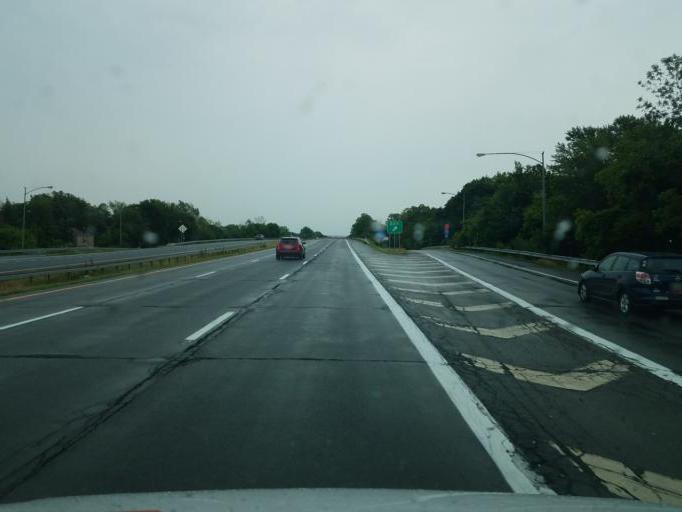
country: US
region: New York
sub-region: Niagara County
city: Niagara Falls
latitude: 43.0797
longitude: -78.9791
